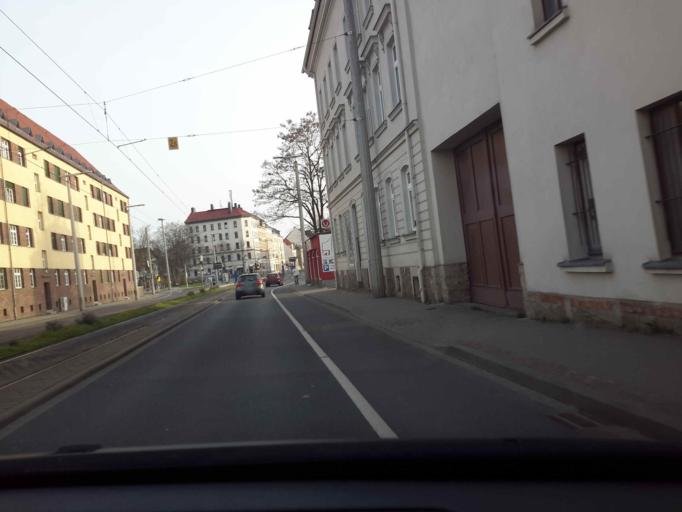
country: DE
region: Saxony
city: Leipzig
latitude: 51.3694
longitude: 12.3859
